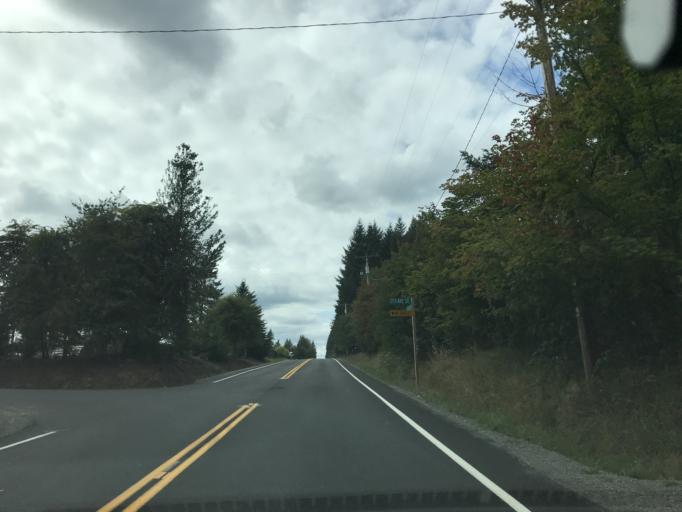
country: US
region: Washington
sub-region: King County
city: Black Diamond
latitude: 47.2868
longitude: -122.0041
